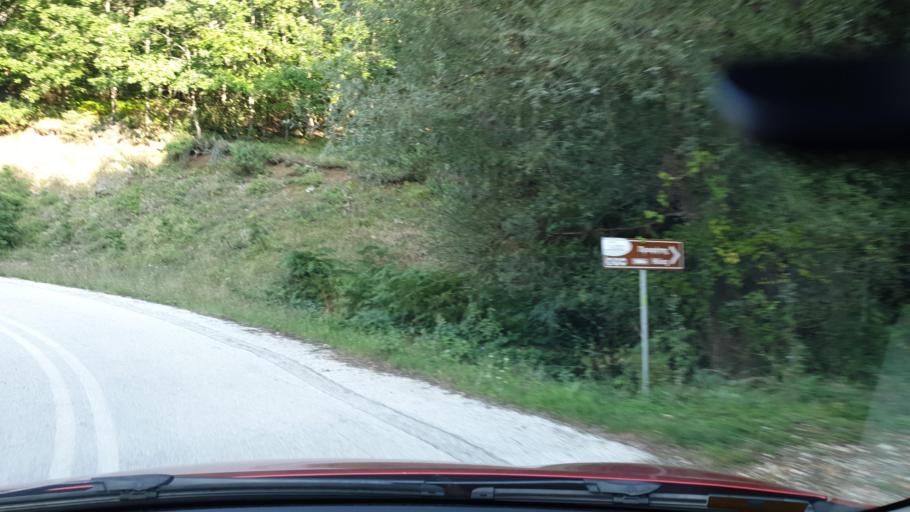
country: GR
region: Central Macedonia
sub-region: Nomos Chalkidikis
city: Galatista
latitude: 40.5053
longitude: 23.2492
